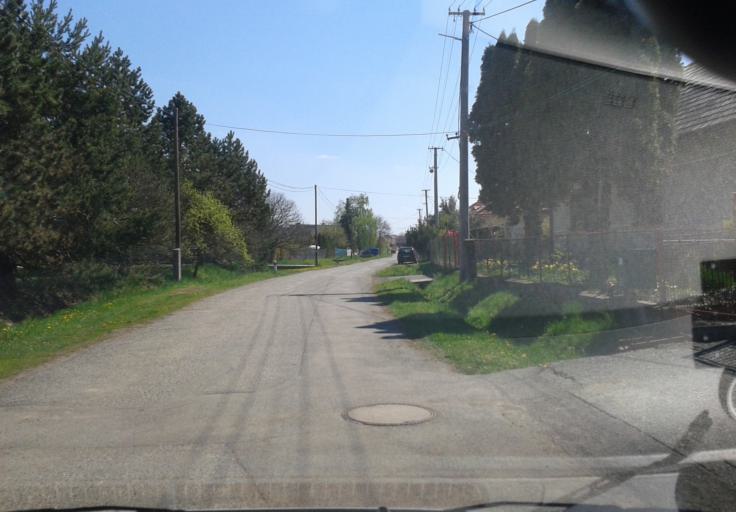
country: SK
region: Nitriansky
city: Levice
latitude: 48.2589
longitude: 18.7275
